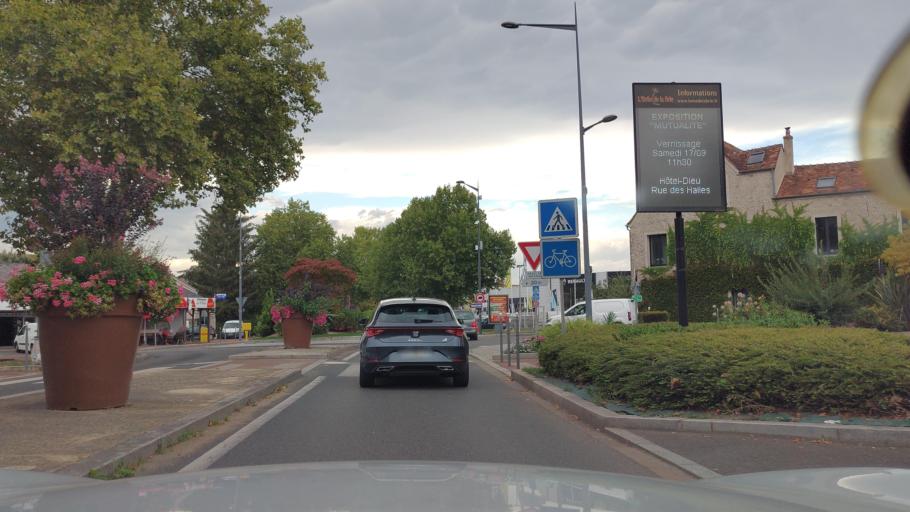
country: FR
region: Ile-de-France
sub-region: Departement de Seine-et-Marne
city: Brie-Comte-Robert
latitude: 48.6963
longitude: 2.6079
